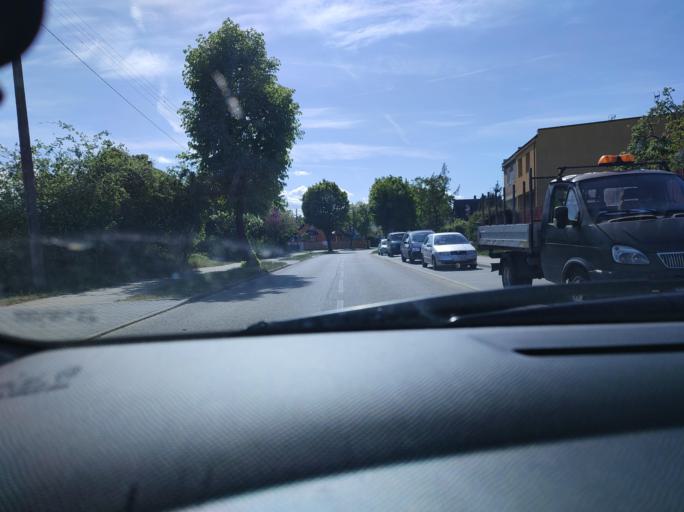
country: PL
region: West Pomeranian Voivodeship
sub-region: Powiat goleniowski
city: Stepnica
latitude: 53.6616
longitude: 14.4983
